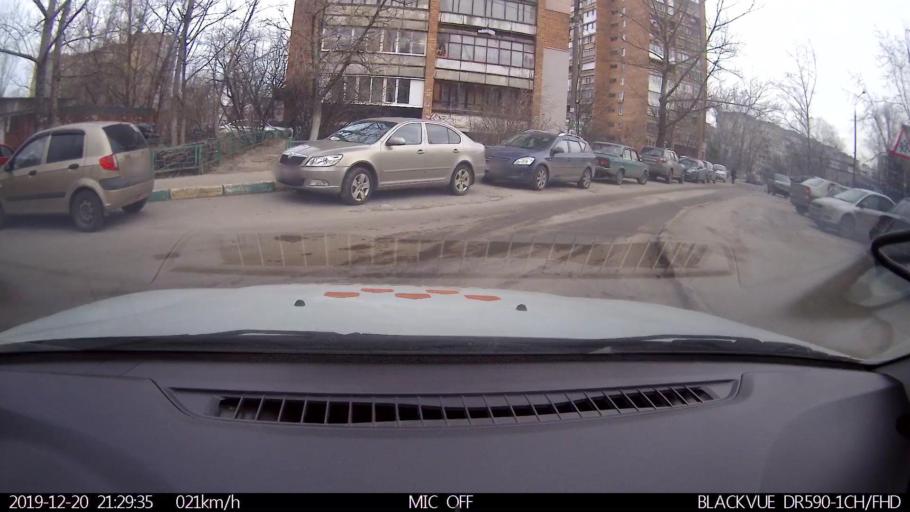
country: RU
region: Nizjnij Novgorod
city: Nizhniy Novgorod
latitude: 56.3328
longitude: 43.9409
